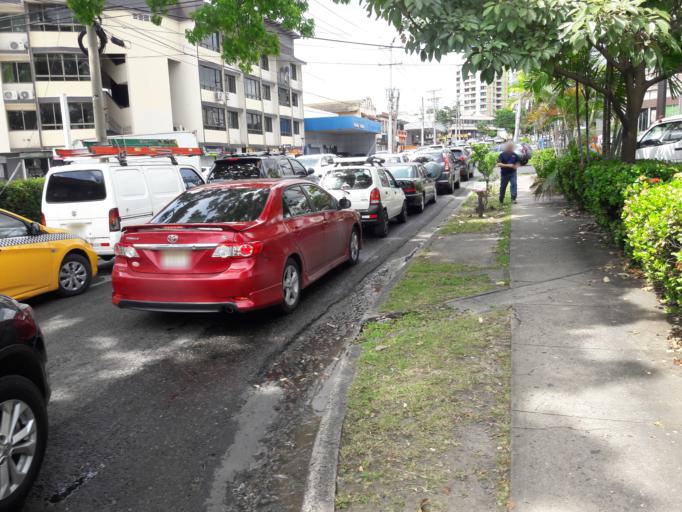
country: PA
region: Panama
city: Panama
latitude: 9.0081
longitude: -79.5057
